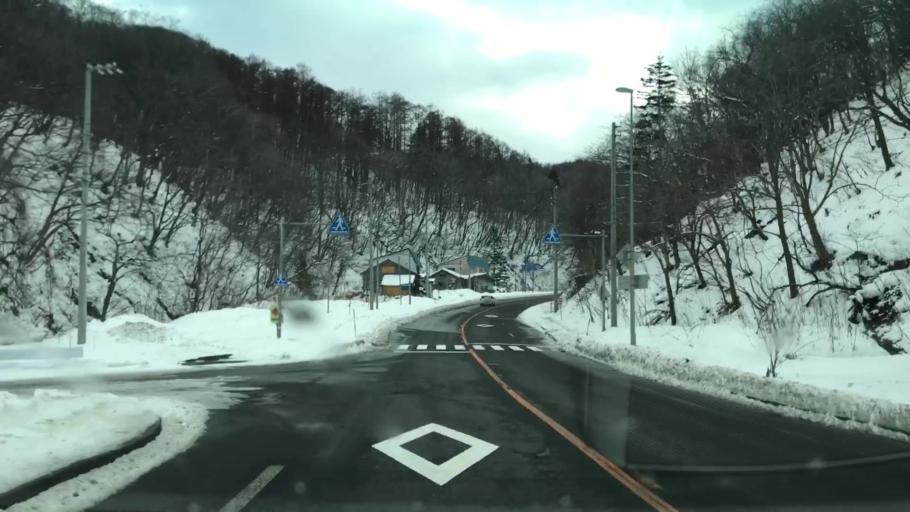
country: JP
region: Hokkaido
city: Yoichi
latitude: 43.2328
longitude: 140.7358
